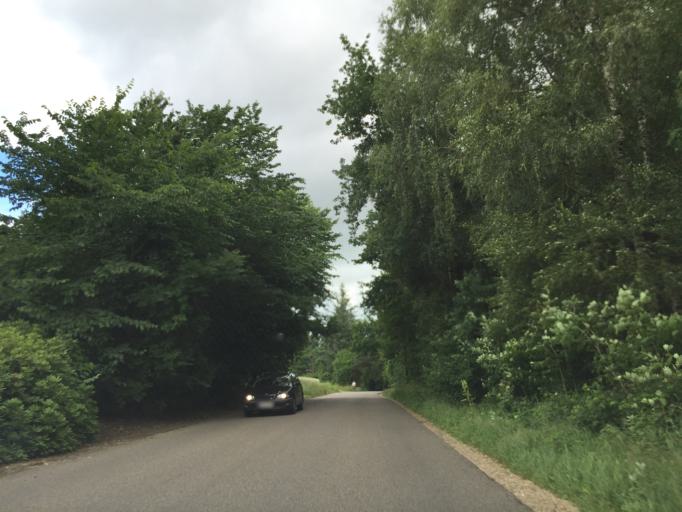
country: DK
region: Central Jutland
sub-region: Silkeborg Kommune
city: Svejbaek
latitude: 56.1719
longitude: 9.6527
